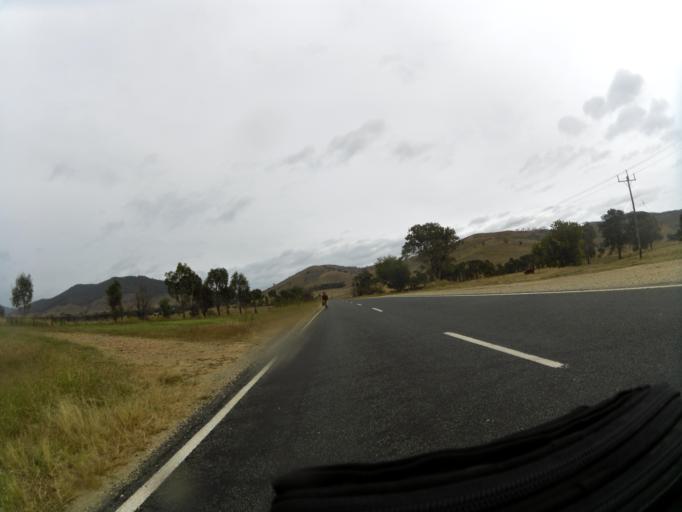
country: AU
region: New South Wales
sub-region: Greater Hume Shire
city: Holbrook
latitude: -36.2038
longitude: 147.7452
